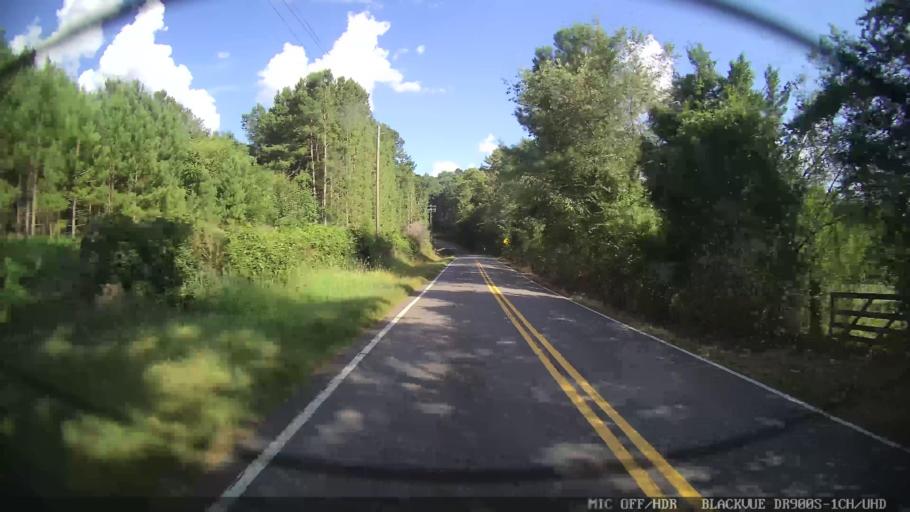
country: US
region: Georgia
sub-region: Floyd County
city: Lindale
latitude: 34.2045
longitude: -85.1177
